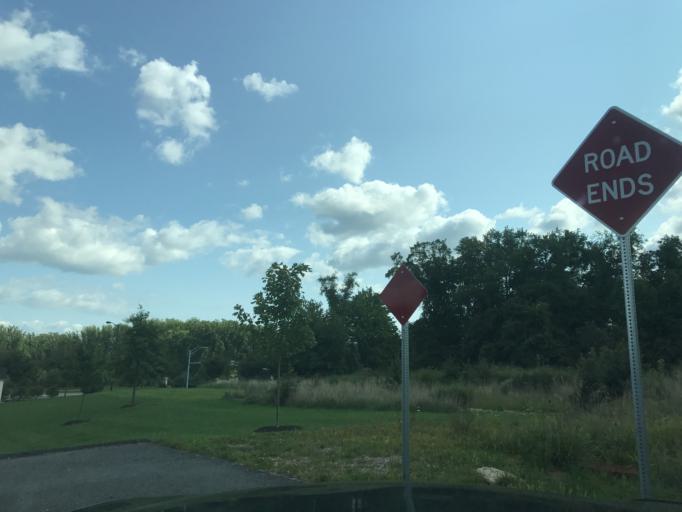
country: US
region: Maryland
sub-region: Baltimore County
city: White Marsh
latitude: 39.3626
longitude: -76.4169
